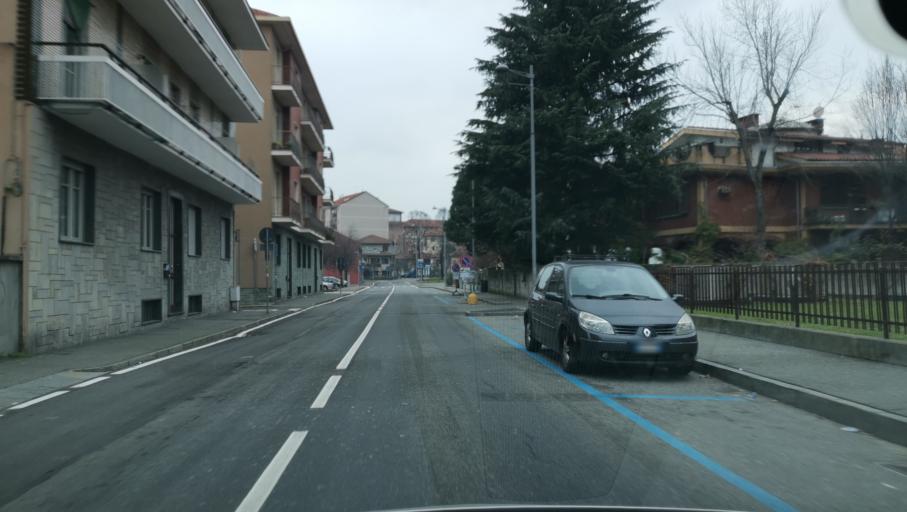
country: IT
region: Piedmont
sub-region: Provincia di Torino
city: Settimo Torinese
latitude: 45.1359
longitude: 7.7748
